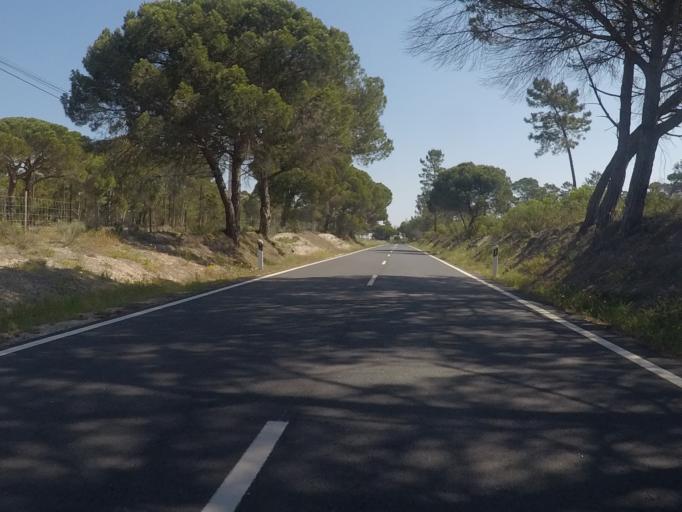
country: PT
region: Setubal
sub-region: Grandola
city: Grandola
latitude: 38.2610
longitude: -8.7324
